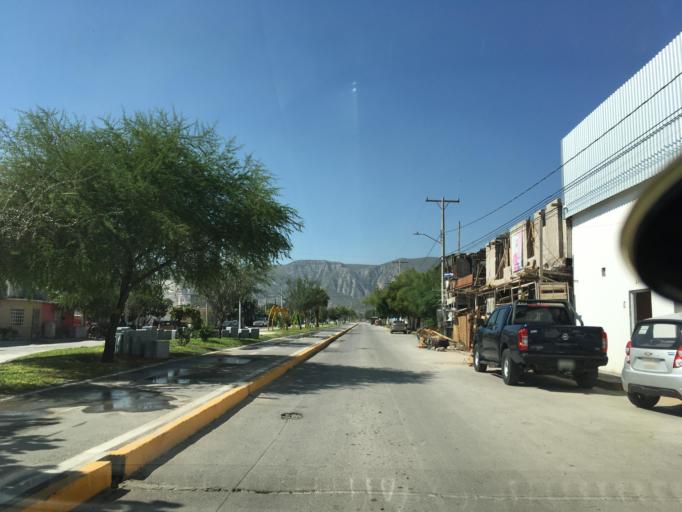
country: MX
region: Coahuila
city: Torreon
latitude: 25.5031
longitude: -103.3941
